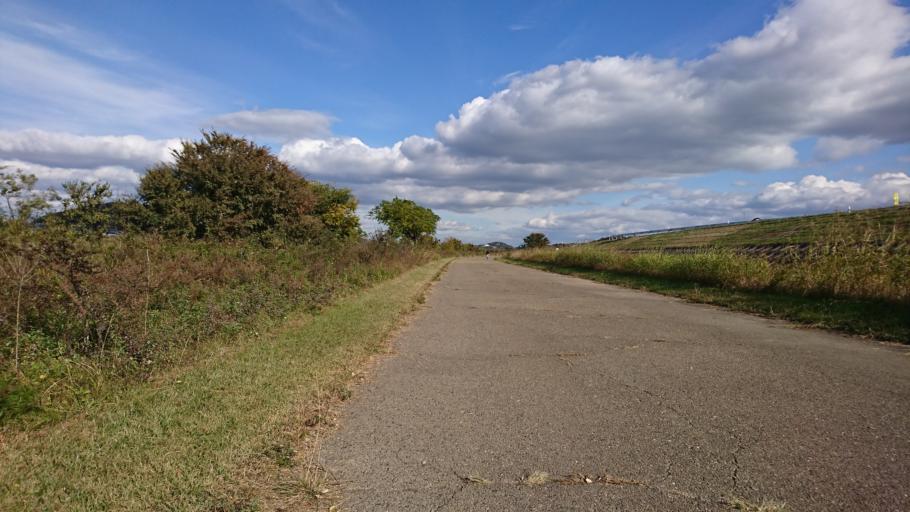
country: JP
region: Hyogo
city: Kakogawacho-honmachi
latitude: 34.7804
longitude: 134.8489
